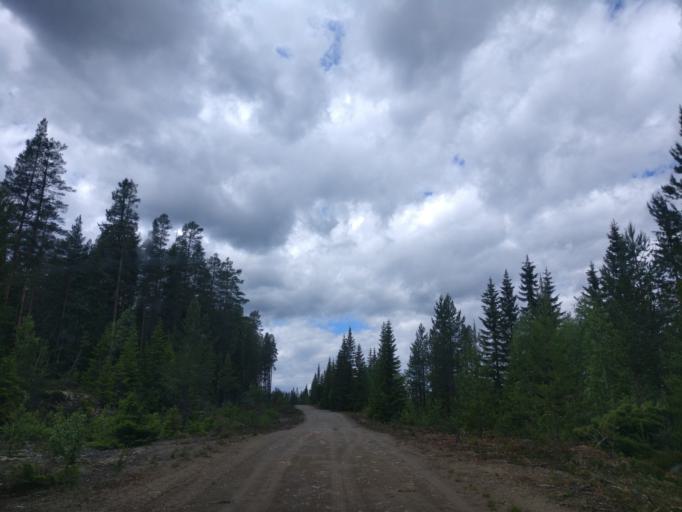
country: SE
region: Jaemtland
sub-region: Harjedalens Kommun
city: Sveg
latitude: 62.1977
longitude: 13.4099
